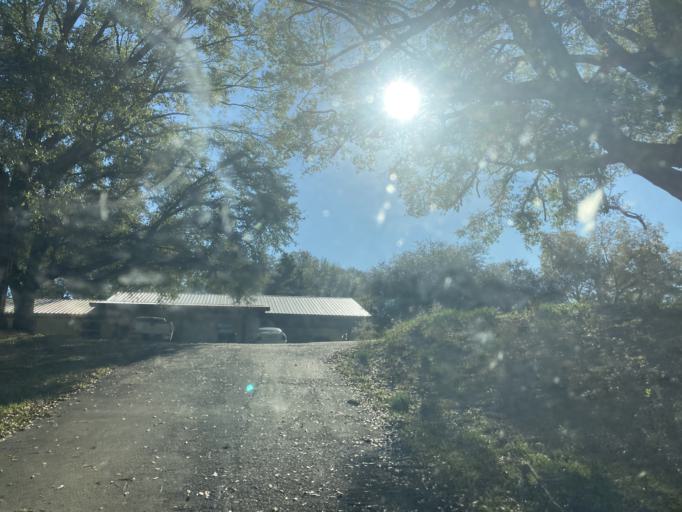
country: US
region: Mississippi
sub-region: Madison County
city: Kearney Park
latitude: 32.7156
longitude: -90.3763
